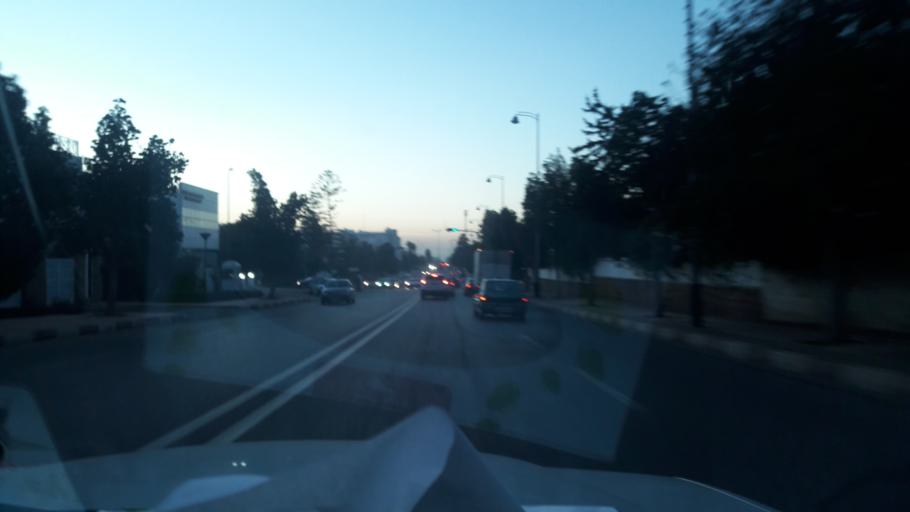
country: MA
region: Rabat-Sale-Zemmour-Zaer
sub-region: Skhirate-Temara
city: Temara
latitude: 33.9304
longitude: -6.9273
